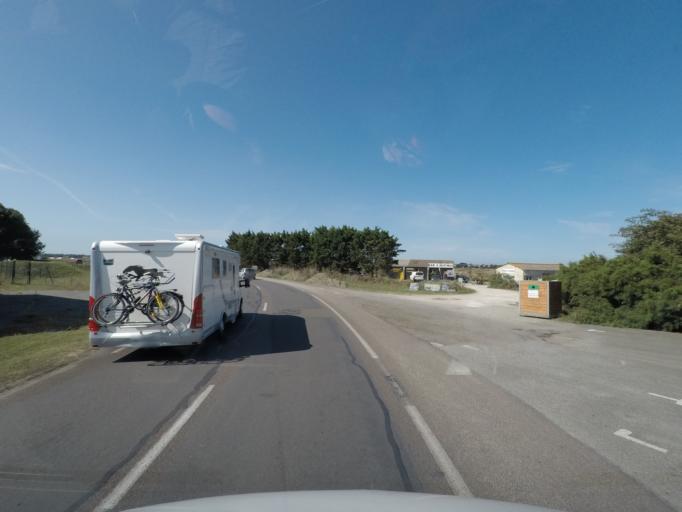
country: FR
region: Pays de la Loire
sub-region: Departement de la Vendee
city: La Gueriniere
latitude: 46.9934
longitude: -2.2492
